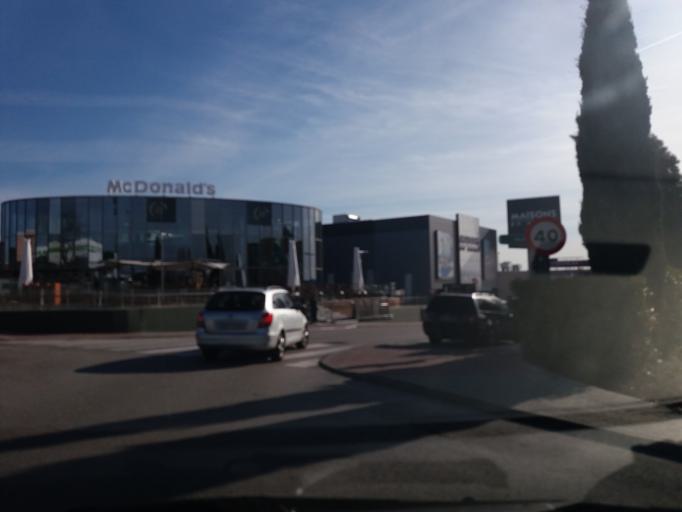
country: ES
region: Madrid
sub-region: Provincia de Madrid
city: Majadahonda
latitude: 40.4559
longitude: -3.8740
